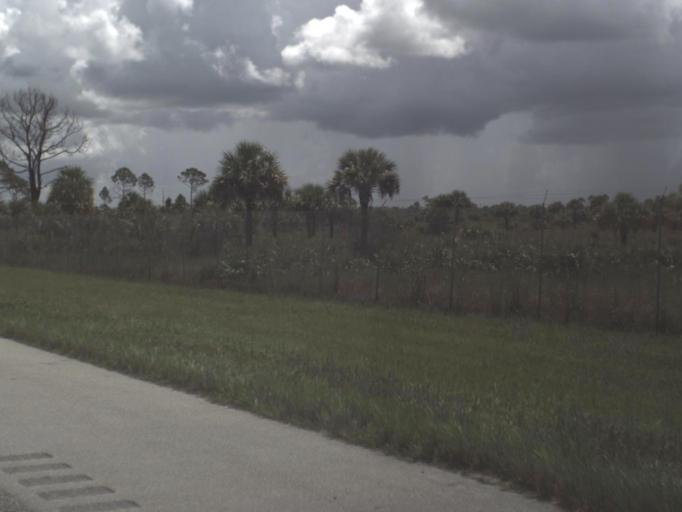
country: US
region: Florida
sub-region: Collier County
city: Immokalee
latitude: 26.1547
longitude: -81.3287
